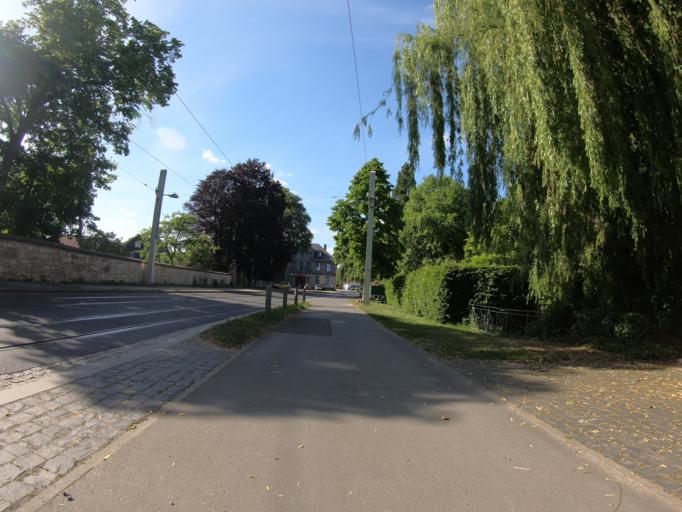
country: DE
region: Lower Saxony
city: Leiferde
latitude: 52.2082
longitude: 10.5247
